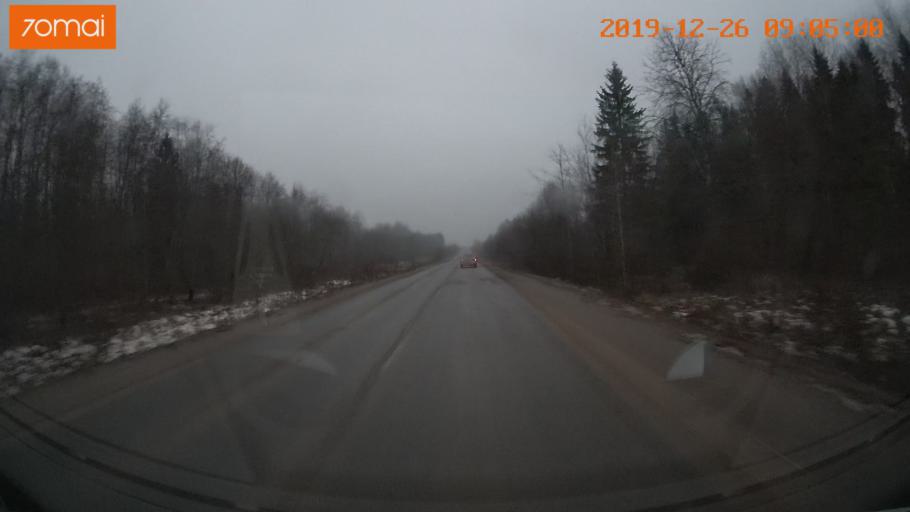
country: RU
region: Vologda
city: Gryazovets
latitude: 58.8211
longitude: 40.2602
